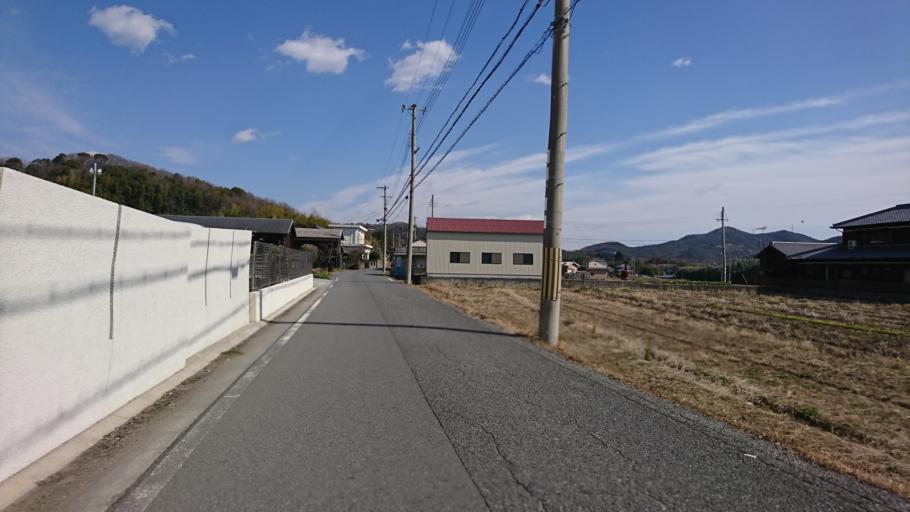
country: JP
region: Hyogo
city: Kakogawacho-honmachi
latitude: 34.8212
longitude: 134.8254
